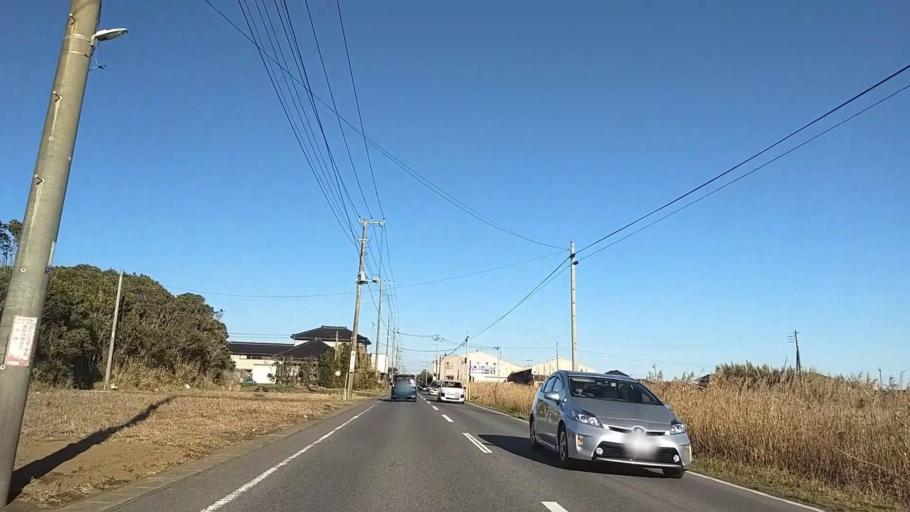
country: JP
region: Chiba
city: Yokaichiba
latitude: 35.6634
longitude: 140.6037
